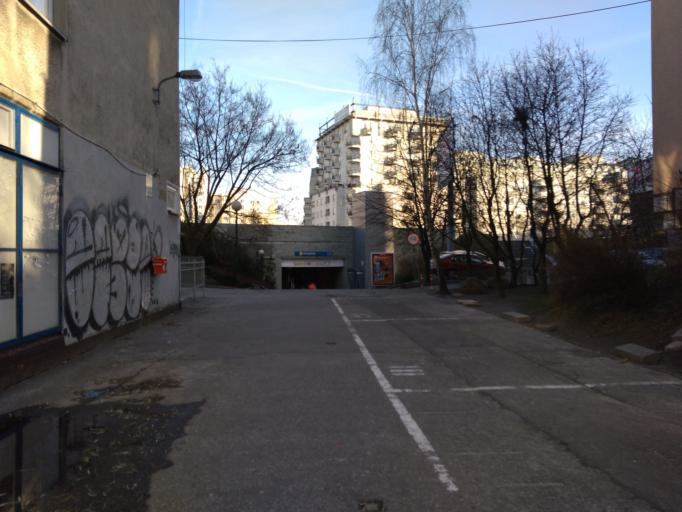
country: PL
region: Masovian Voivodeship
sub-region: Warszawa
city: Ursynow
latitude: 52.1612
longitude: 21.0270
